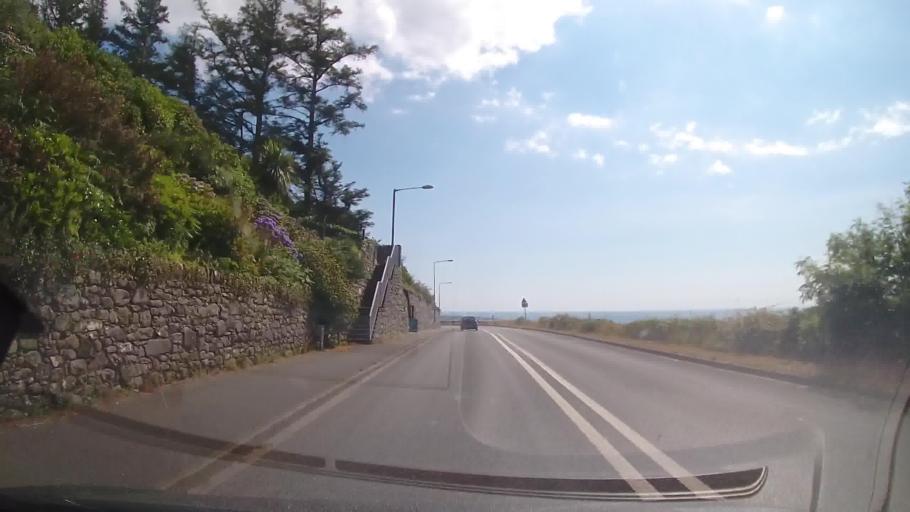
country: GB
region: Wales
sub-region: Gwynedd
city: Llanfair
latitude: 52.8453
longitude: -4.1172
